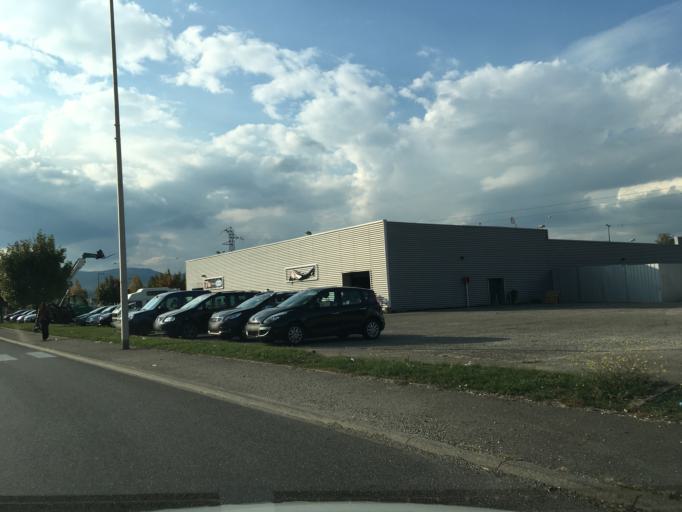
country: FR
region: Alsace
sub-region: Departement du Haut-Rhin
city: Colmar
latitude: 48.0913
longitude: 7.3509
